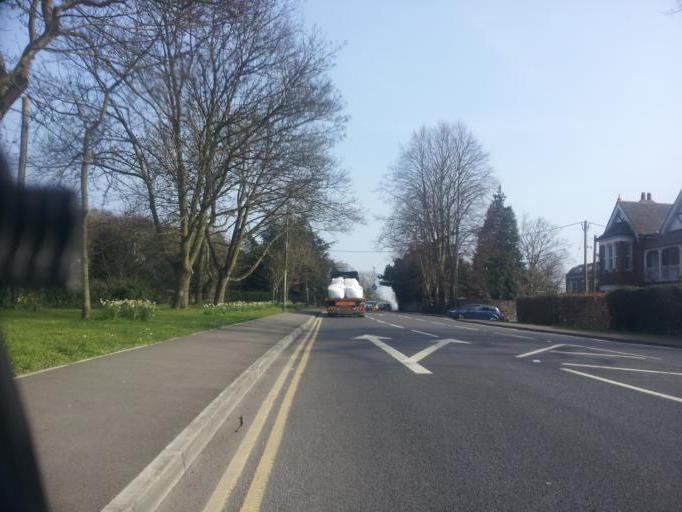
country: GB
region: England
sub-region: Medway
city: Cuxton
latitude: 51.4120
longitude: 0.4569
